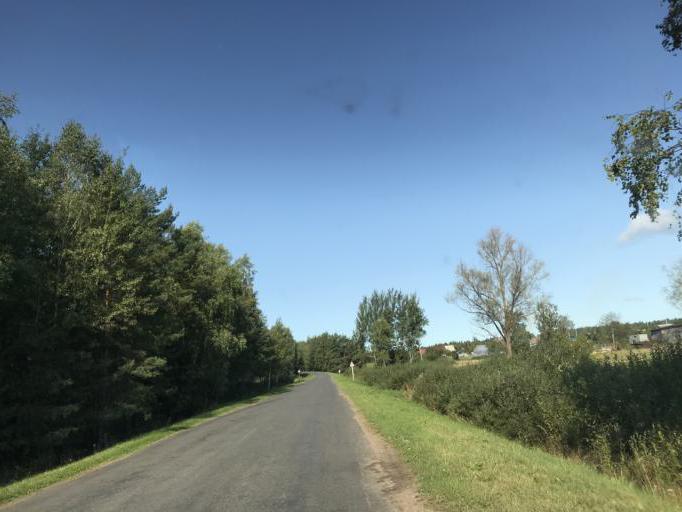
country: BY
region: Mogilev
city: Myazhysyatki
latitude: 53.7955
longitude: 30.1917
